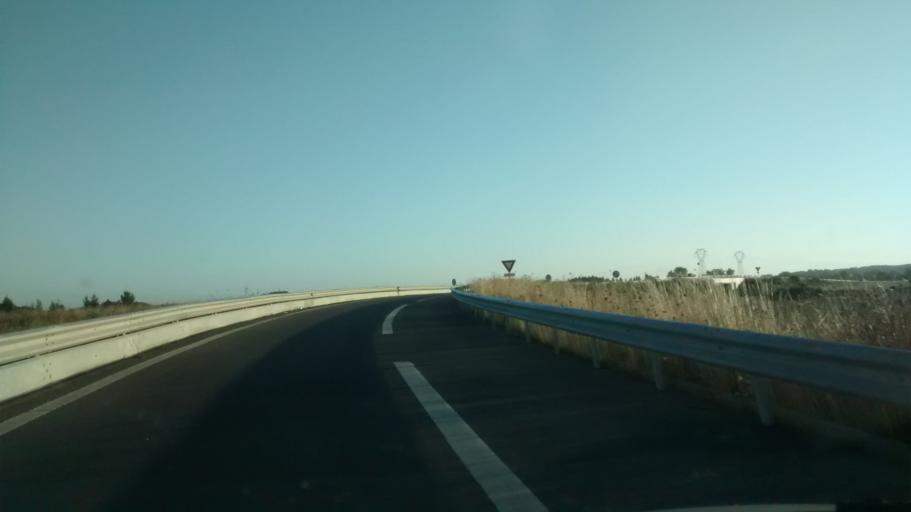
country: FR
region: Brittany
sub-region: Departement d'Ille-et-Vilaine
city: Miniac-Morvan
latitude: 48.5424
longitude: -1.9201
